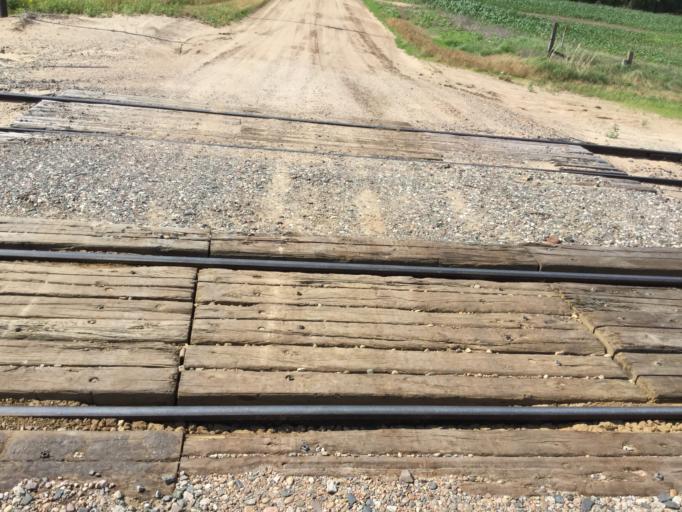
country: US
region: Kansas
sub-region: Pawnee County
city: Larned
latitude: 37.9516
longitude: -99.1138
